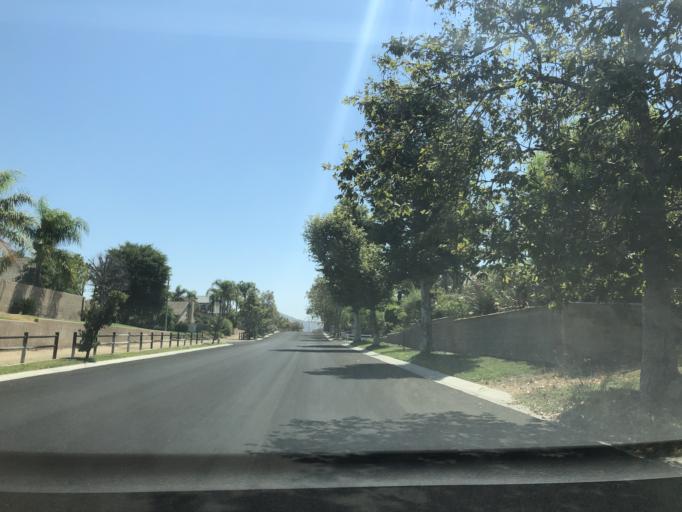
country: US
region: California
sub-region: Riverside County
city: Norco
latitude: 33.9152
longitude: -117.5765
